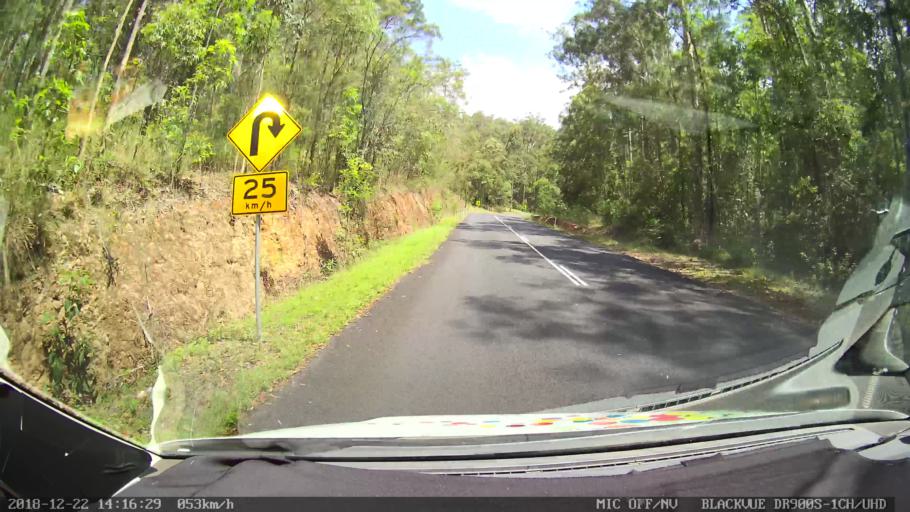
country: AU
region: New South Wales
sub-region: Clarence Valley
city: Coutts Crossing
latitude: -30.0052
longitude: 152.6715
